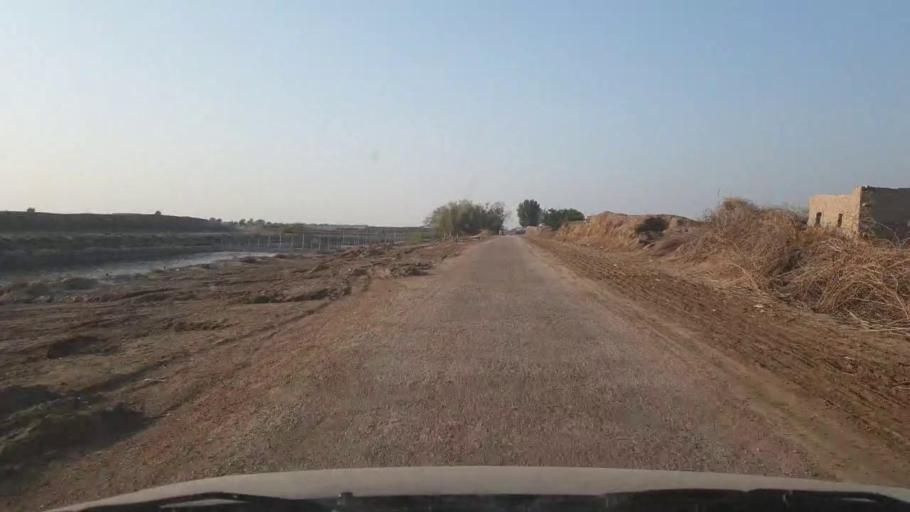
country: PK
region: Sindh
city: Samaro
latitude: 25.2891
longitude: 69.3340
